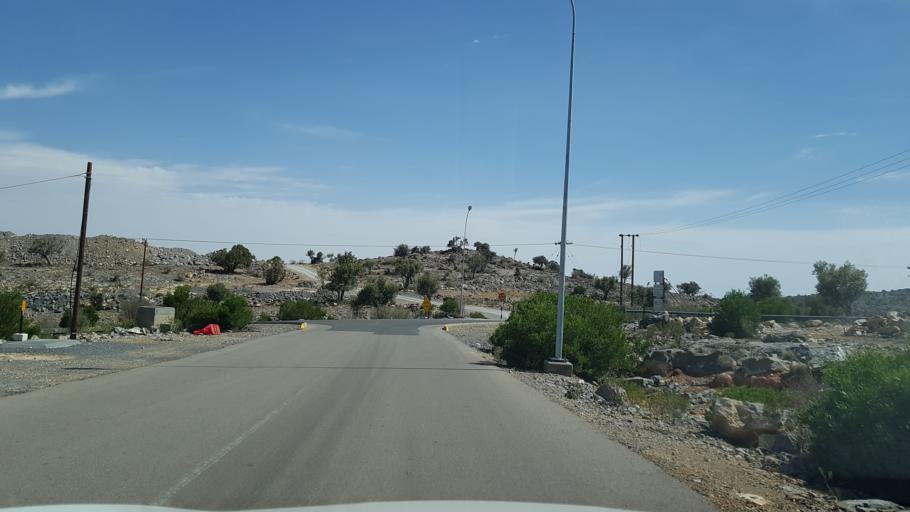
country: OM
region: Muhafazat ad Dakhiliyah
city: Nizwa
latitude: 23.1194
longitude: 57.6033
